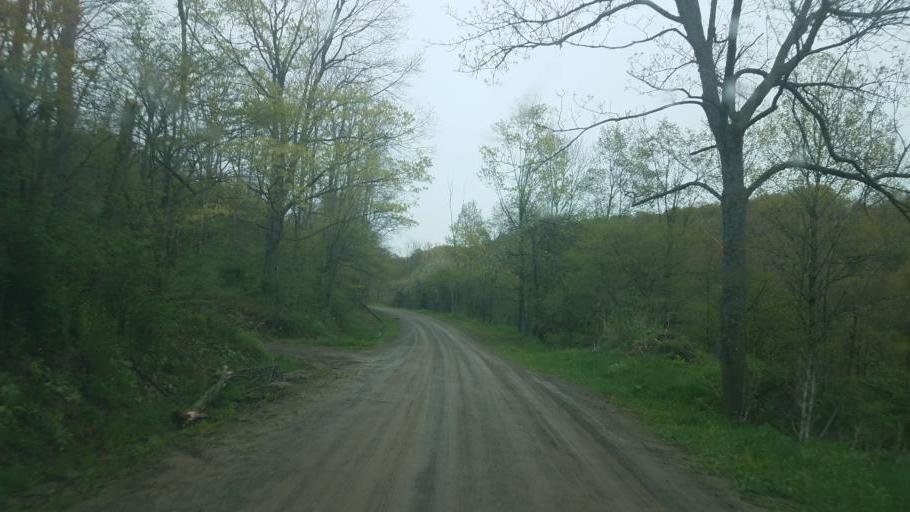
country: US
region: New York
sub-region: Allegany County
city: Andover
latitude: 41.9377
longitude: -77.7974
